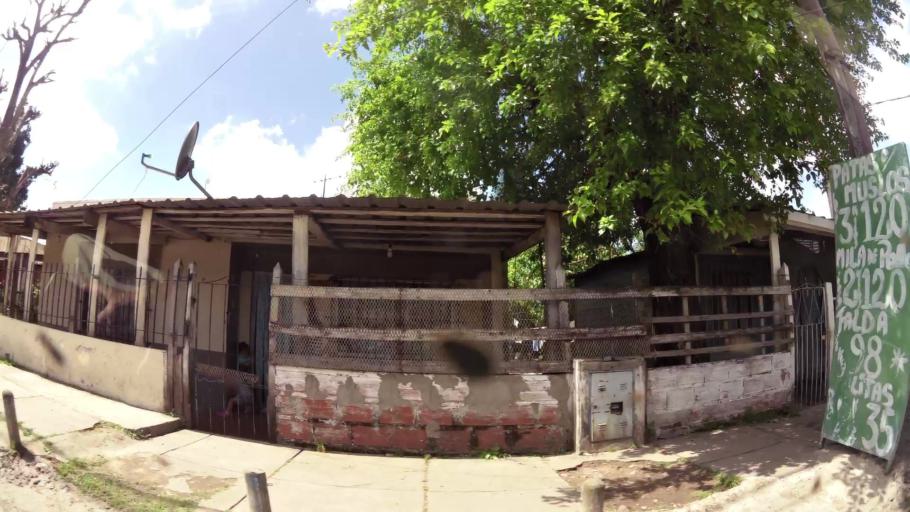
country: AR
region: Buenos Aires
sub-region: Partido de Quilmes
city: Quilmes
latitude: -34.8058
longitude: -58.2471
